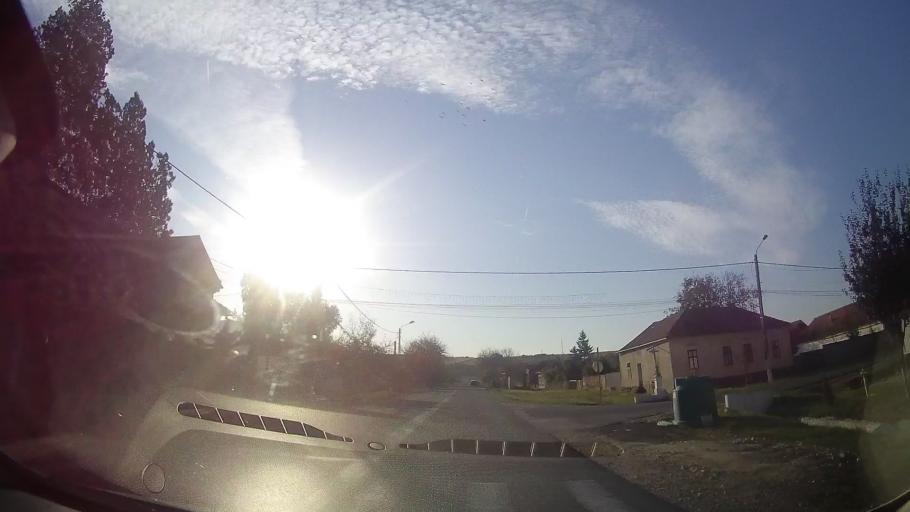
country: RO
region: Timis
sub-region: Comuna Masloc
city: Masloc
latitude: 45.9668
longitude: 21.4798
